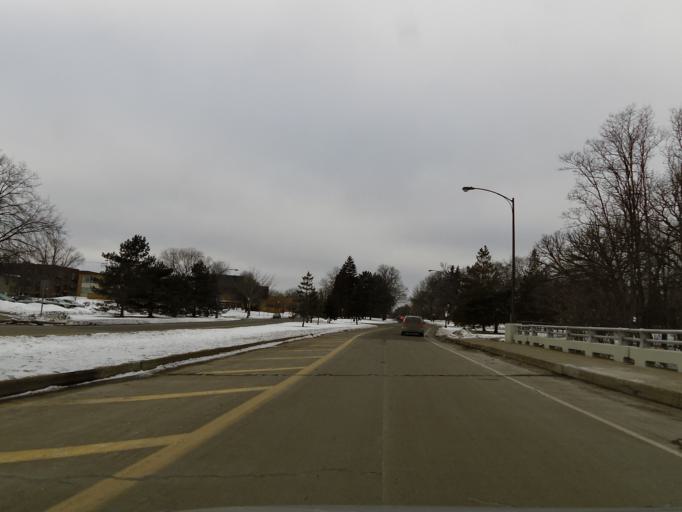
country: US
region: Minnesota
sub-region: Ramsey County
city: Falcon Heights
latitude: 44.9415
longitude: -93.1529
